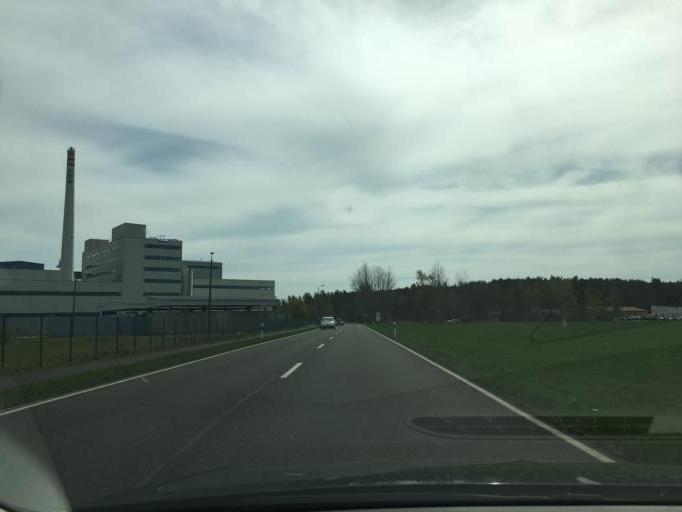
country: DE
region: Brandenburg
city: Tschernitz
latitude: 51.5768
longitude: 14.6007
